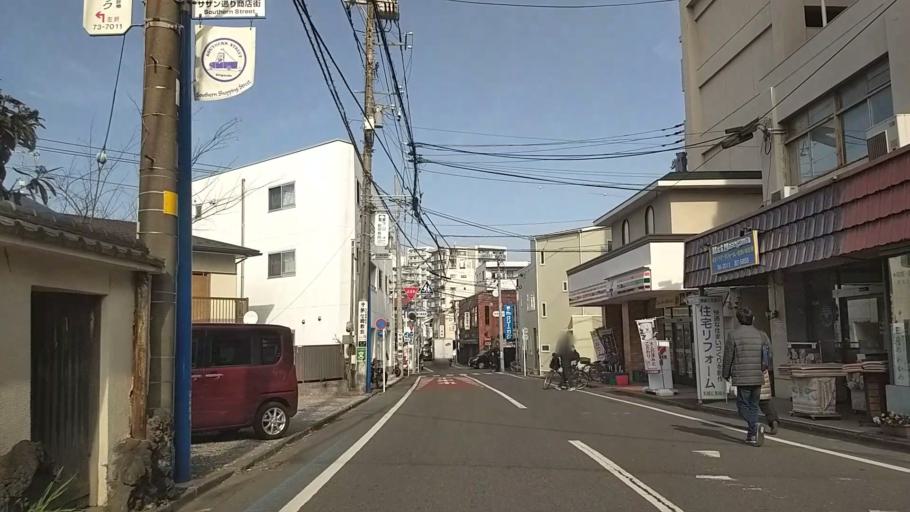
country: JP
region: Kanagawa
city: Chigasaki
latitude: 35.3267
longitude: 139.4031
